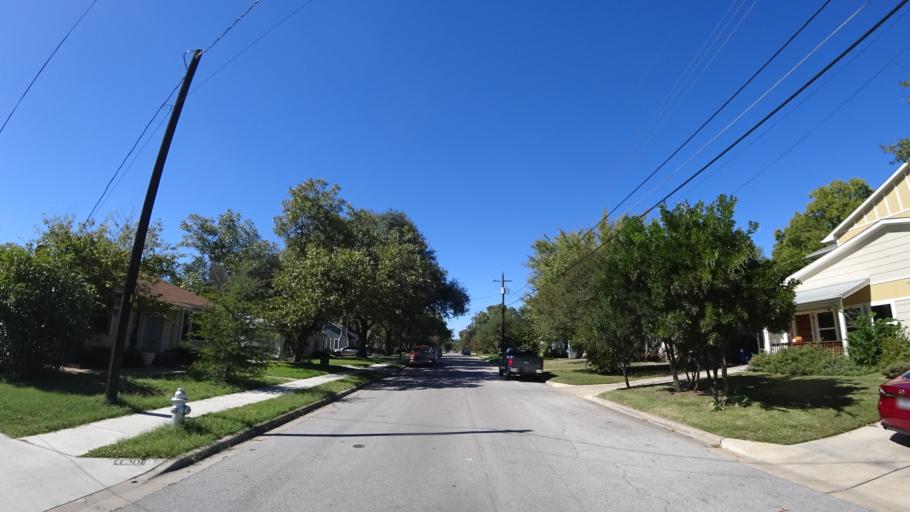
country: US
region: Texas
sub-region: Travis County
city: Austin
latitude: 30.3350
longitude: -97.7277
